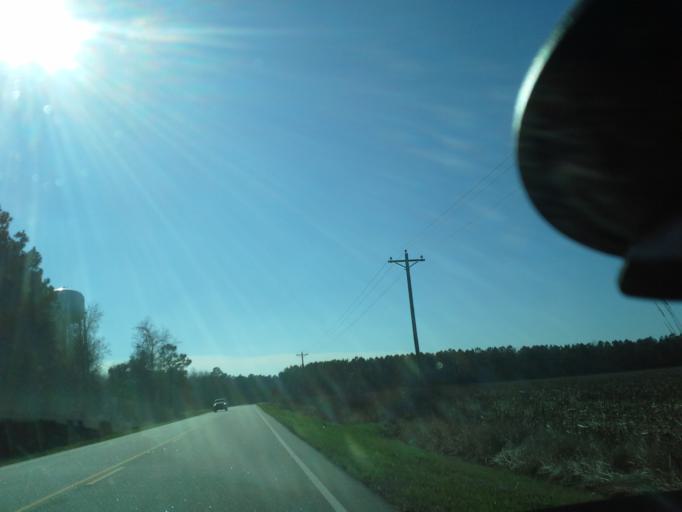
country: US
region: North Carolina
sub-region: Beaufort County
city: Belhaven
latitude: 35.5759
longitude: -76.6868
